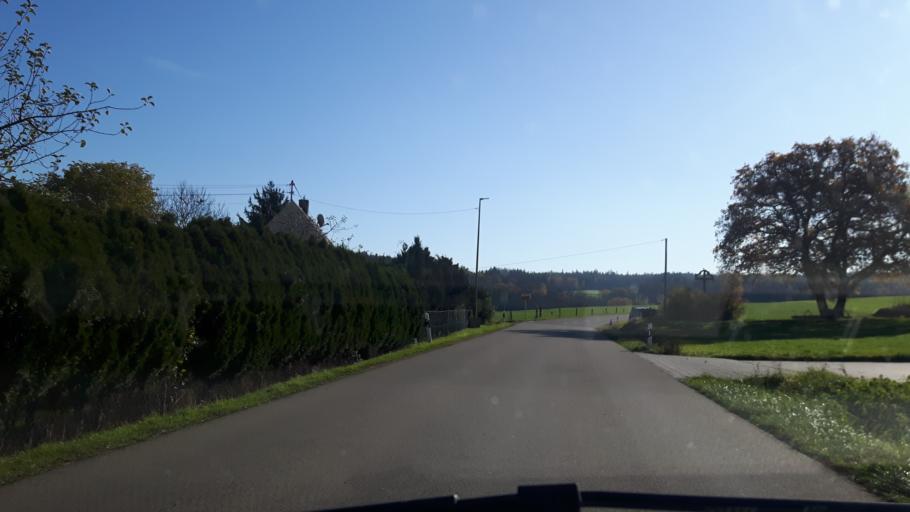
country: DE
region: Bavaria
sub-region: Swabia
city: Marxheim
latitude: 48.7782
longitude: 10.9563
